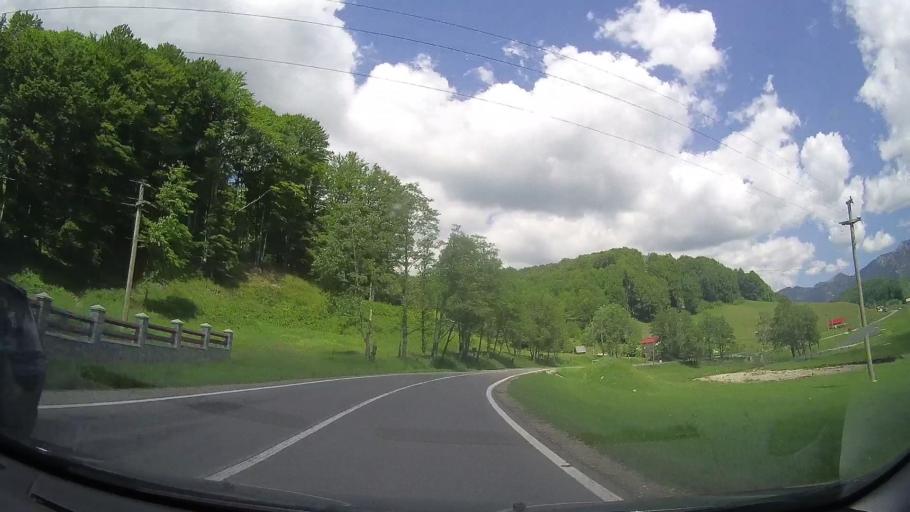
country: RO
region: Prahova
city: Maneciu
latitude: 45.4357
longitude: 25.9368
